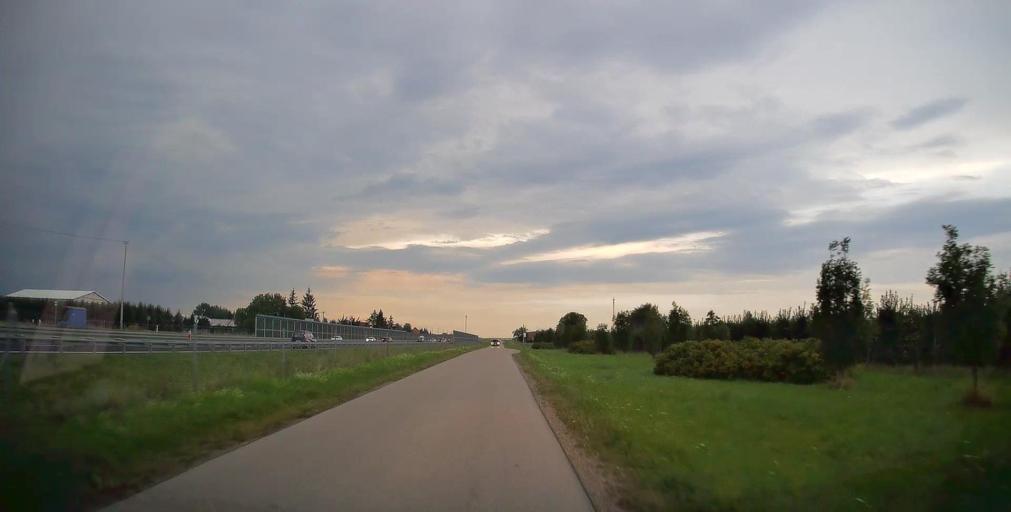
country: PL
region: Masovian Voivodeship
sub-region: Powiat grojecki
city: Goszczyn
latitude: 51.7690
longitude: 20.9008
